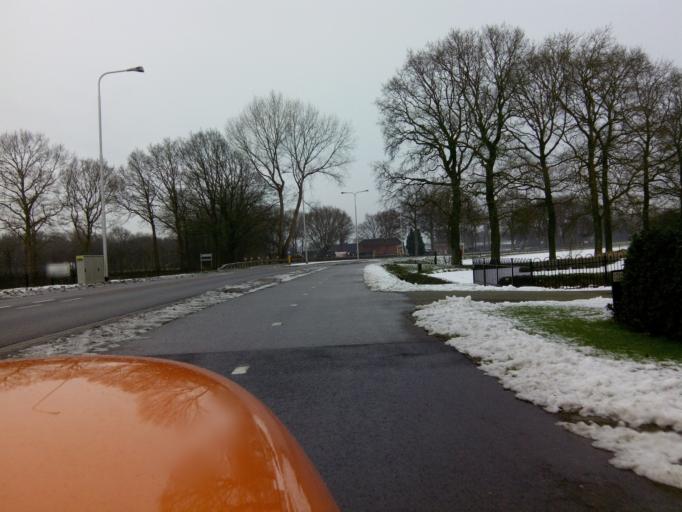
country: NL
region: Gelderland
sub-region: Gemeente Putten
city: Putten
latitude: 52.2233
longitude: 5.6071
